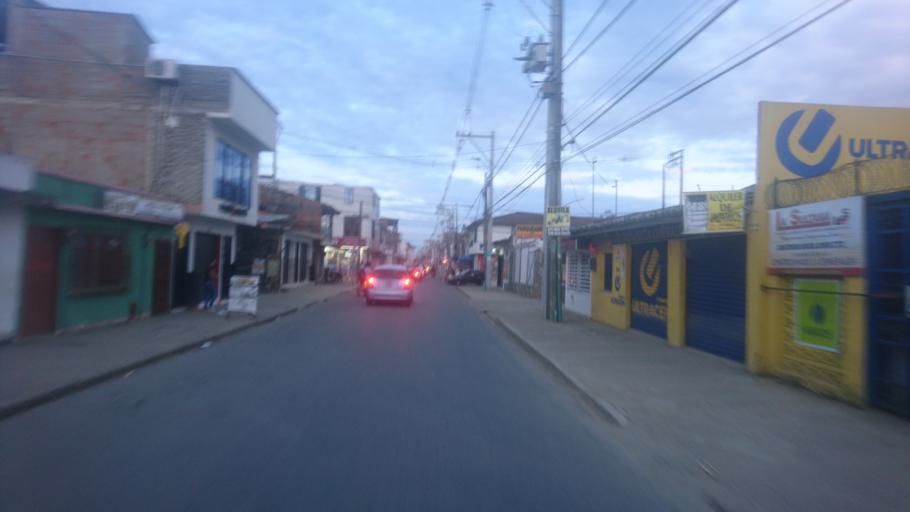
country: CO
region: Valle del Cauca
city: Jamundi
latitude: 3.2598
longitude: -76.5424
